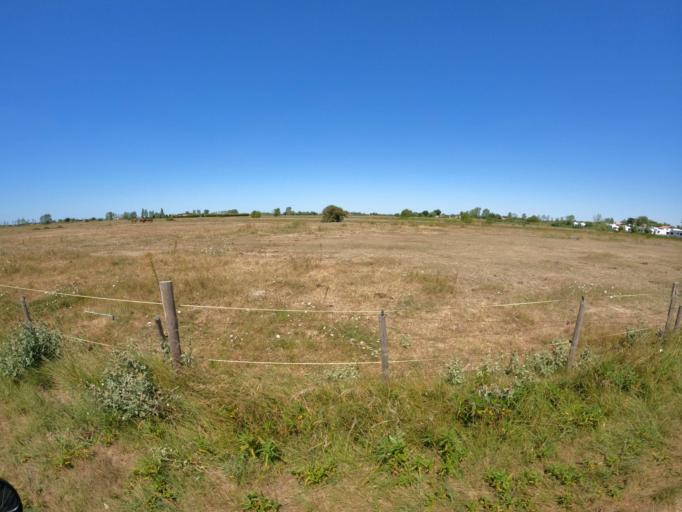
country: FR
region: Pays de la Loire
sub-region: Departement de la Vendee
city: Saint-Jean-de-Monts
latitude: 46.8009
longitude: -2.0709
